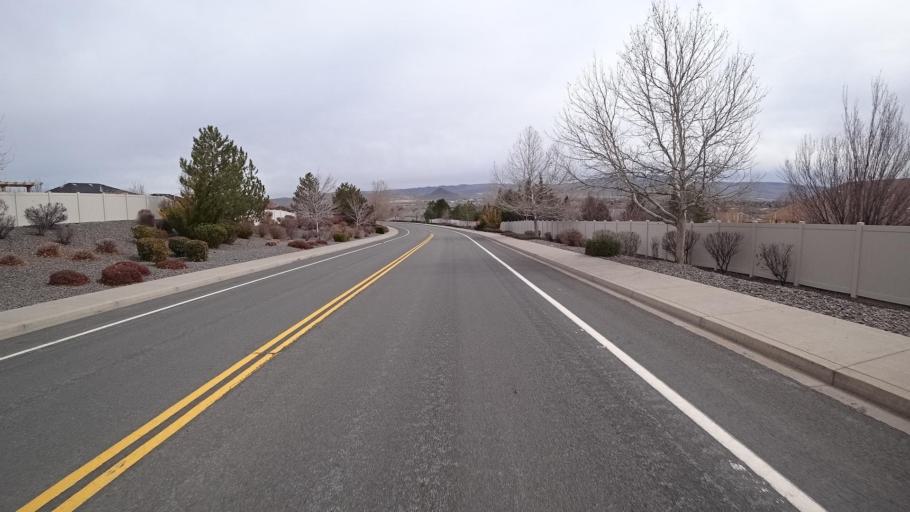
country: US
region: Nevada
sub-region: Washoe County
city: Spanish Springs
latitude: 39.6571
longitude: -119.7303
